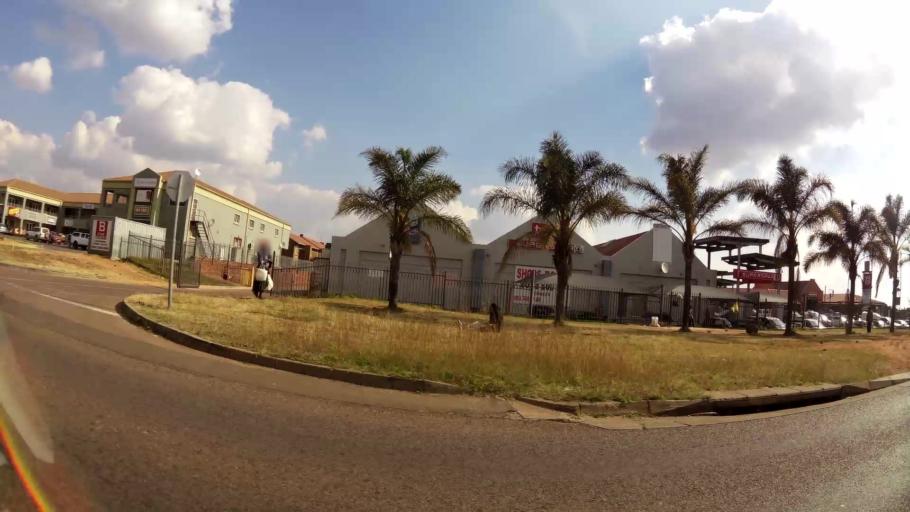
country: ZA
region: Gauteng
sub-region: City of Tshwane Metropolitan Municipality
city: Centurion
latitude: -25.8416
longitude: 28.2442
